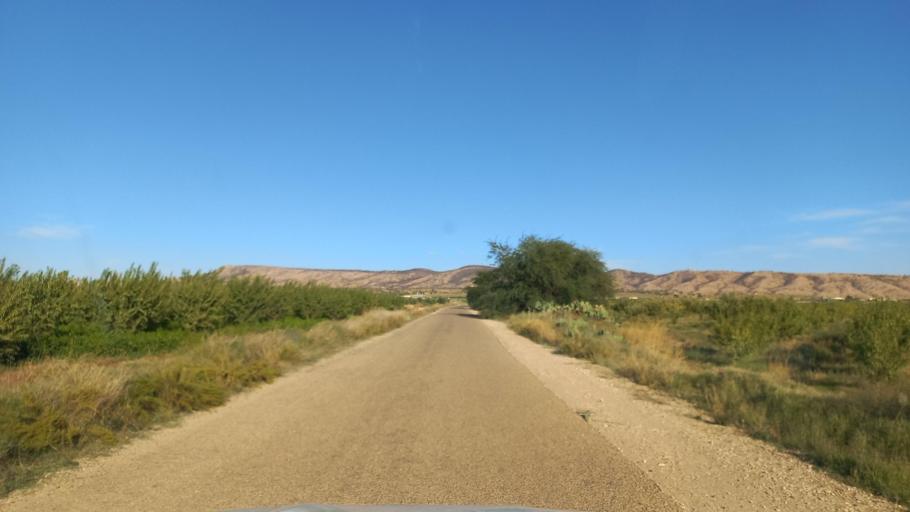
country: TN
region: Al Qasrayn
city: Sbiba
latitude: 35.3369
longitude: 9.1128
